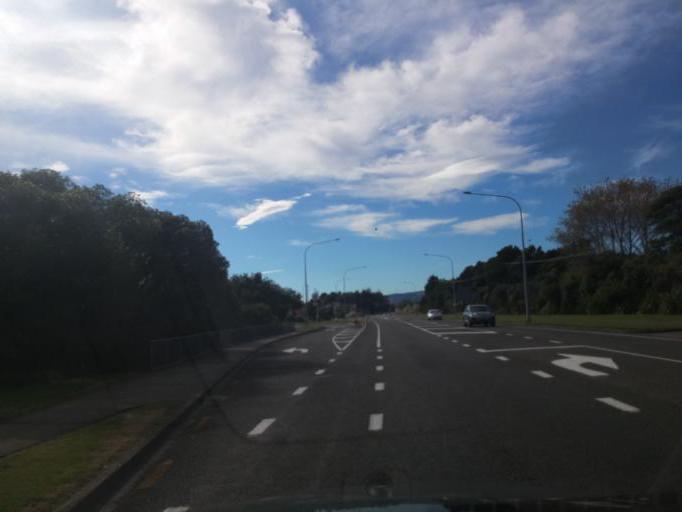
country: NZ
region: Manawatu-Wanganui
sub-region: Palmerston North City
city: Palmerston North
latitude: -40.3883
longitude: 175.6376
